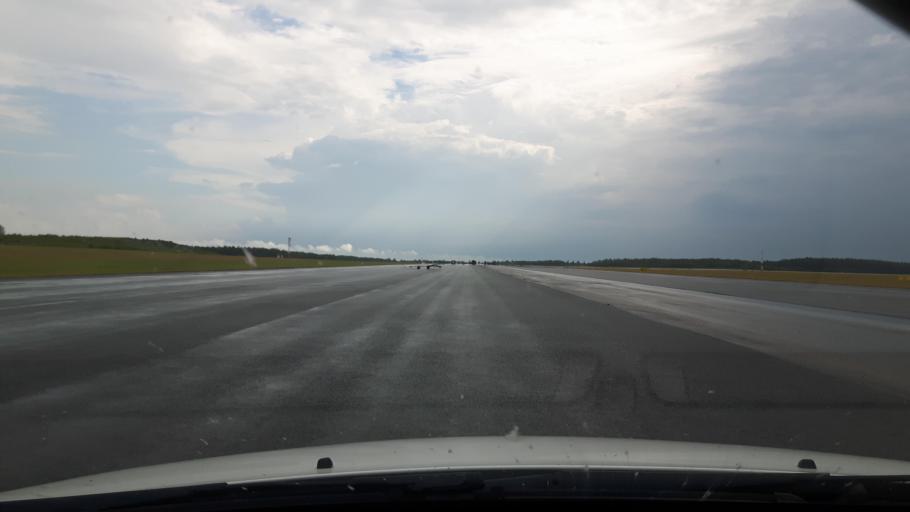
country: SE
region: Stockholm
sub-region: Sigtuna Kommun
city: Rosersberg
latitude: 59.6340
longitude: 17.9535
